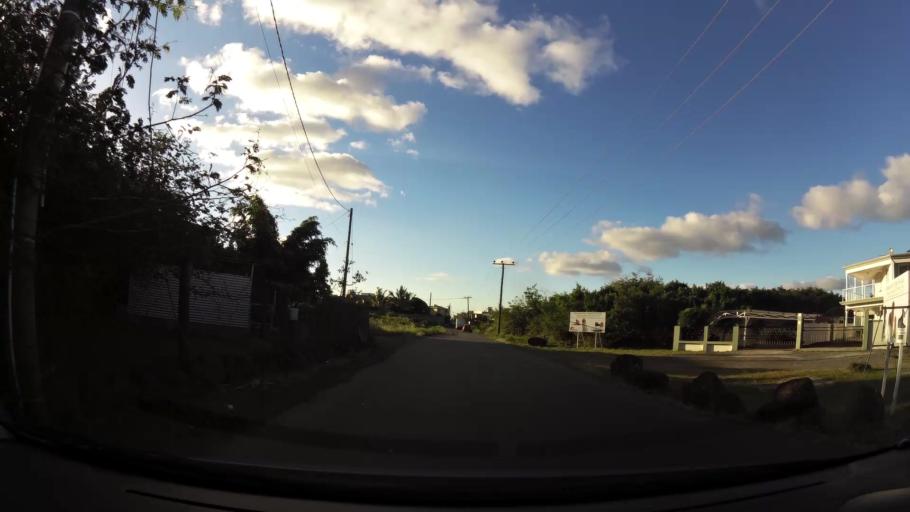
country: MU
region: Plaines Wilhems
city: Quatre Bornes
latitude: -20.2570
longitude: 57.4617
